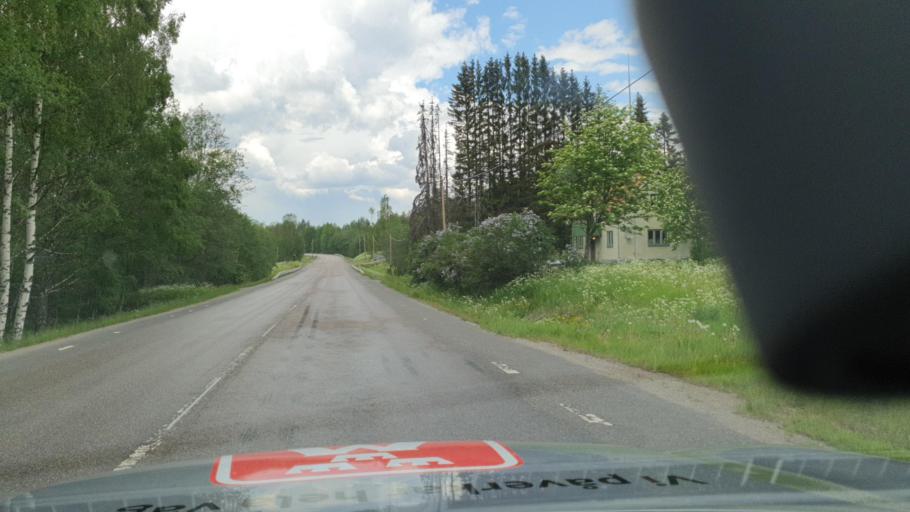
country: SE
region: Vaesternorrland
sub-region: Solleftea Kommun
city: Solleftea
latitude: 63.1882
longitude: 17.2447
